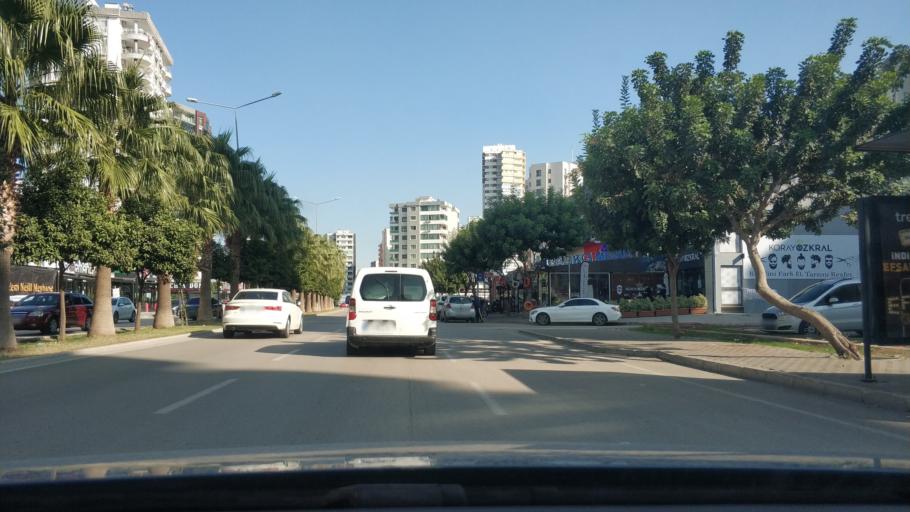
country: TR
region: Adana
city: Seyhan
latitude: 37.0218
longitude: 35.2769
